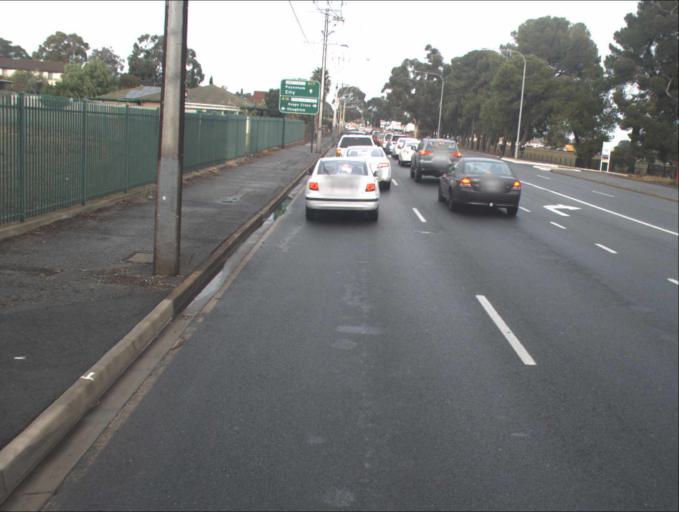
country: AU
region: South Australia
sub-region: Salisbury
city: Ingle Farm
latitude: -34.8448
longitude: 138.6192
